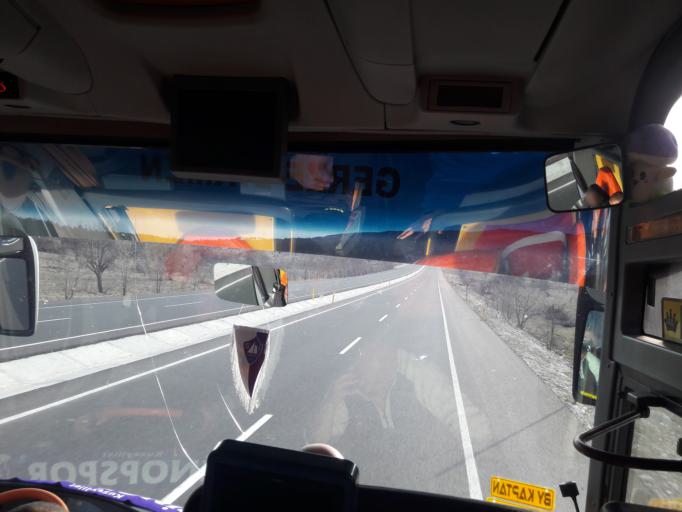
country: TR
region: Cankiri
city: Beloren
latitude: 40.8415
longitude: 33.5802
